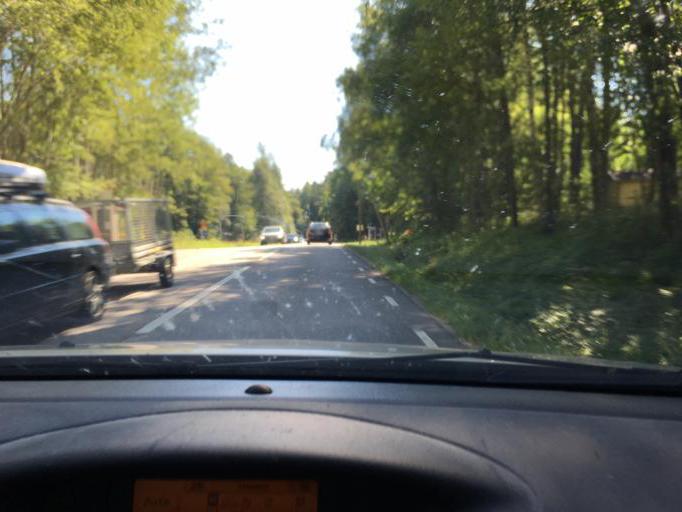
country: SE
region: Stockholm
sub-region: Varmdo Kommun
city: Mortnas
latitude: 59.2797
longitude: 18.4399
